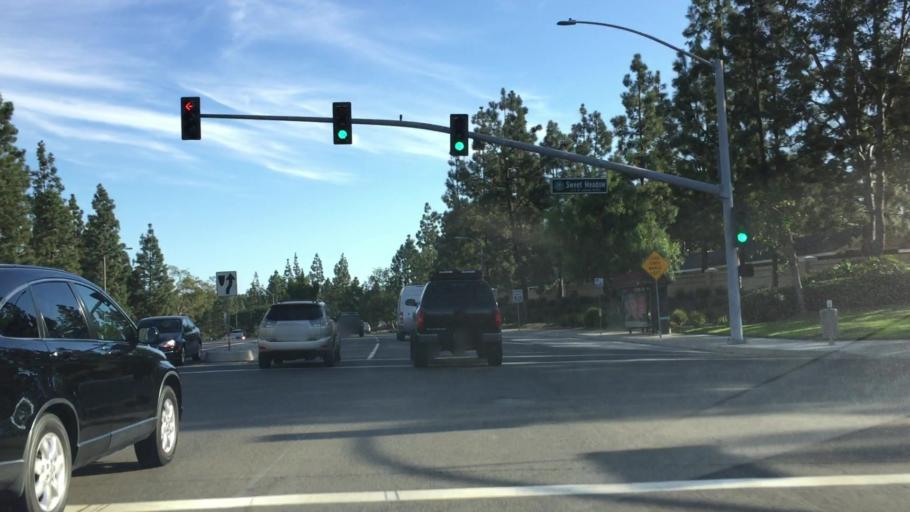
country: US
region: California
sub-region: Orange County
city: Laguna Niguel
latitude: 33.5222
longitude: -117.6858
